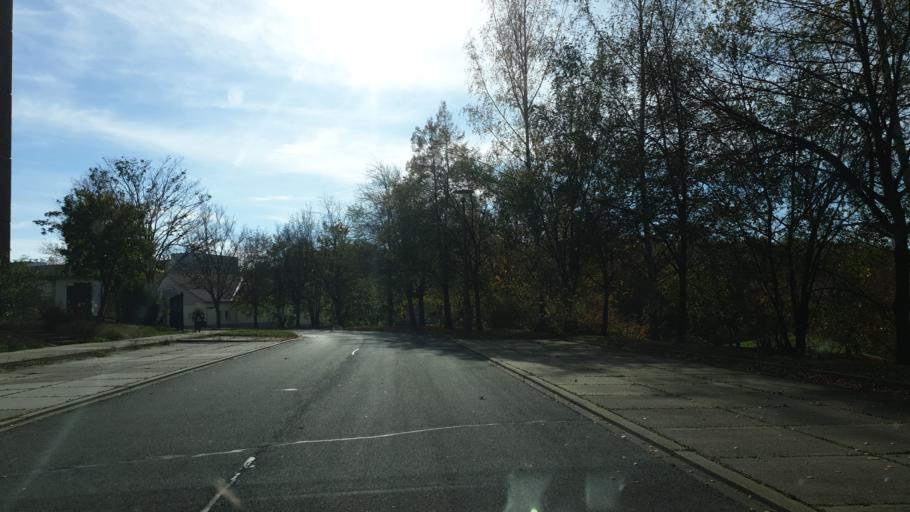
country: DE
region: Thuringia
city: Gera
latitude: 50.9047
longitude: 12.0908
